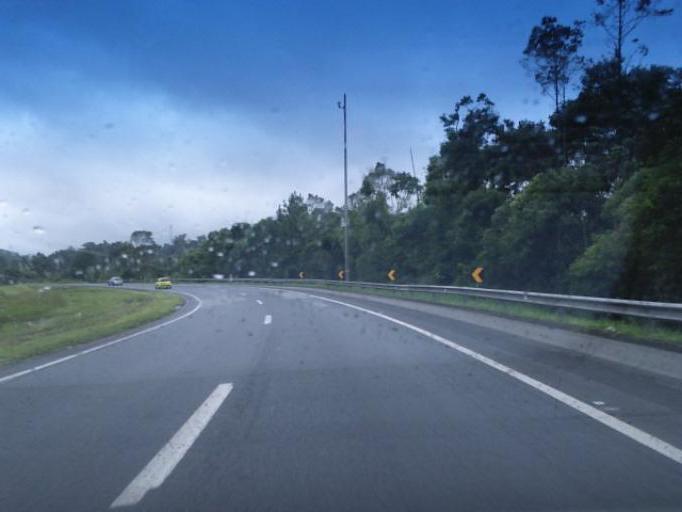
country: BR
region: Parana
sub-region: Antonina
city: Antonina
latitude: -25.0741
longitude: -48.5873
